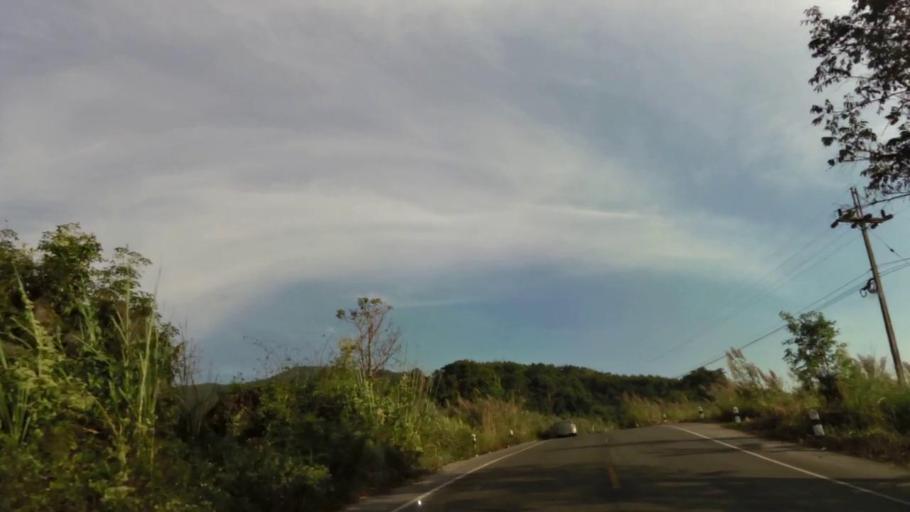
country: TH
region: Chiang Rai
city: Khun Tan
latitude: 19.8645
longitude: 100.4227
